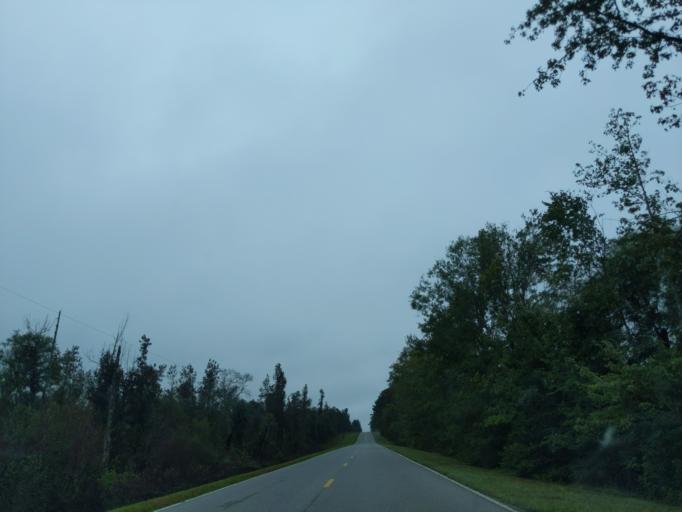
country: US
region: Florida
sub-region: Jackson County
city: Sneads
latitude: 30.6537
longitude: -84.9368
